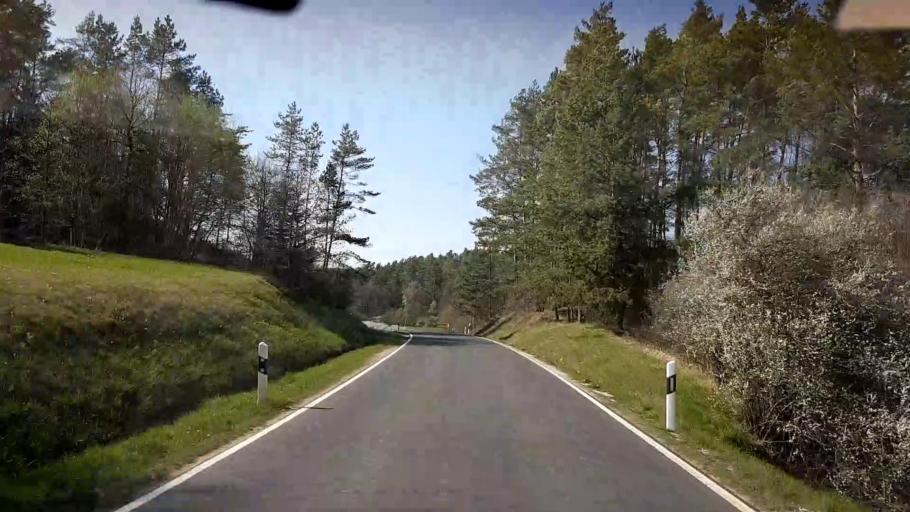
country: DE
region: Bavaria
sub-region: Upper Franconia
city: Waischenfeld
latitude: 49.8068
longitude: 11.3696
